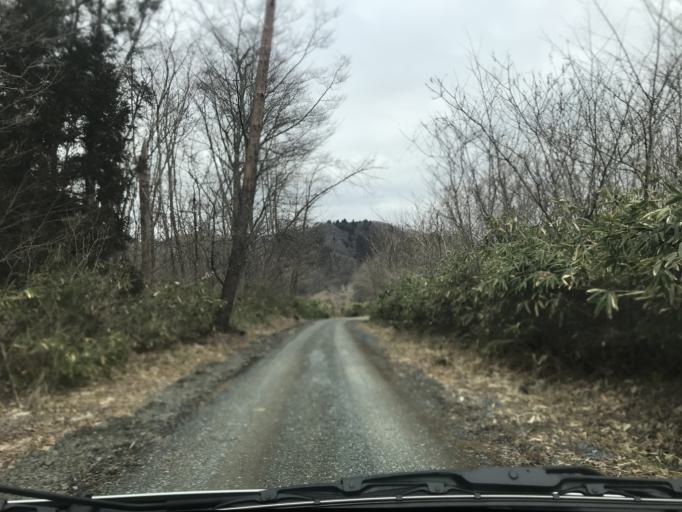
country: JP
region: Iwate
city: Kitakami
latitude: 39.3182
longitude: 141.2273
